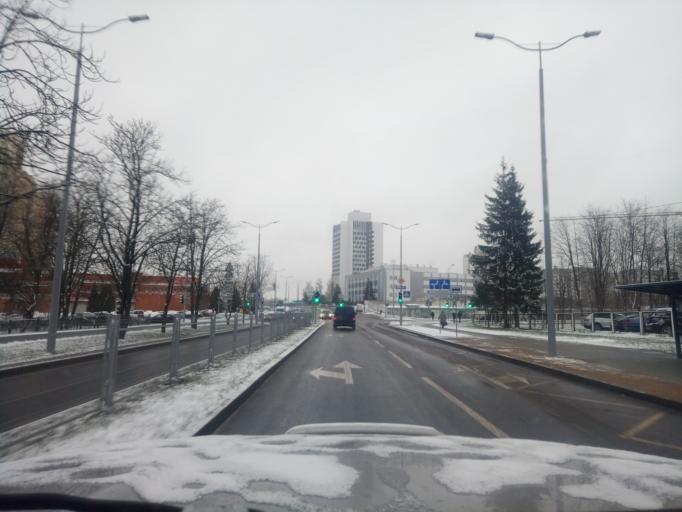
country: BY
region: Minsk
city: Minsk
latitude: 53.9205
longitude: 27.6264
